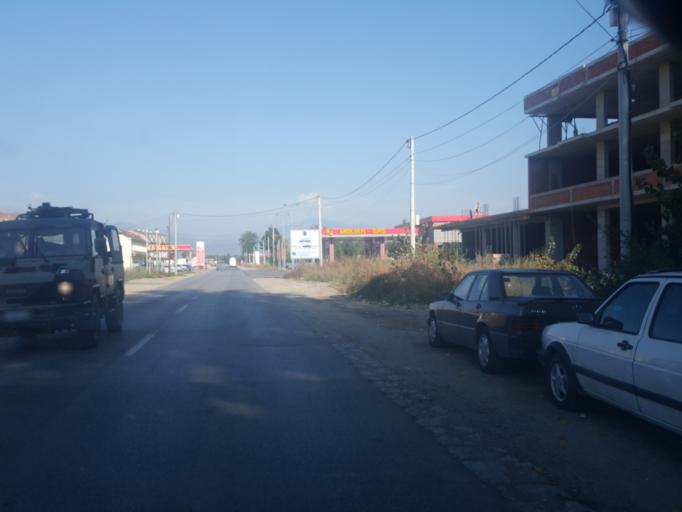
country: XK
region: Gjakova
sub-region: Komuna e Gjakoves
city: Gjakove
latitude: 42.4083
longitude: 20.4064
